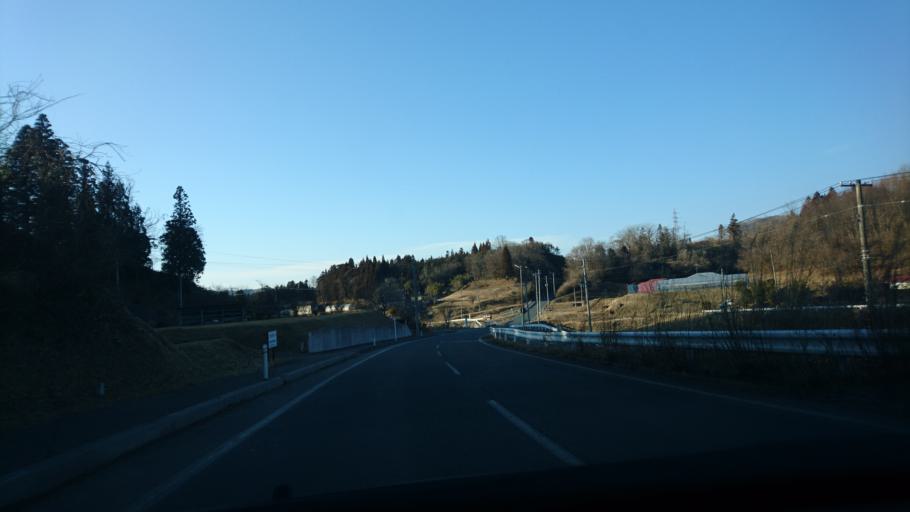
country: JP
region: Iwate
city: Ichinoseki
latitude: 38.9312
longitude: 141.3598
